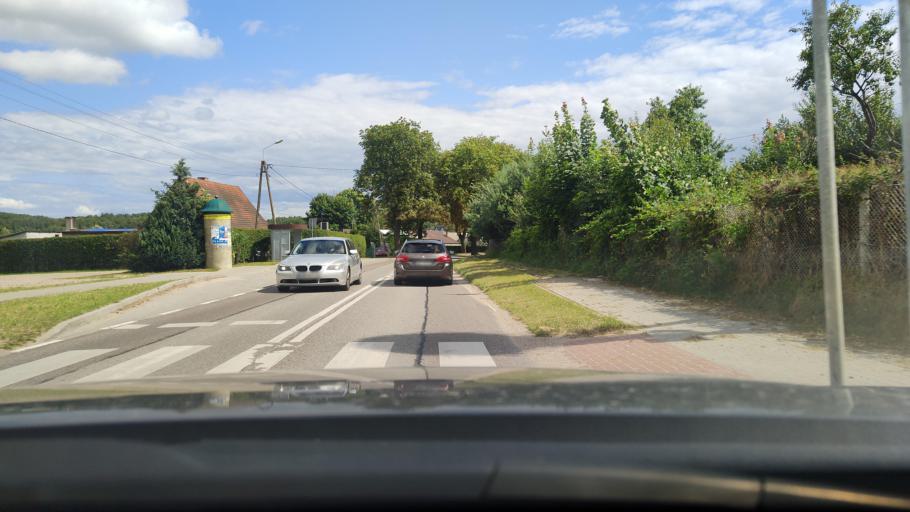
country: PL
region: Pomeranian Voivodeship
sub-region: Powiat wejherowski
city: Koleczkowo
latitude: 54.5417
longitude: 18.2895
